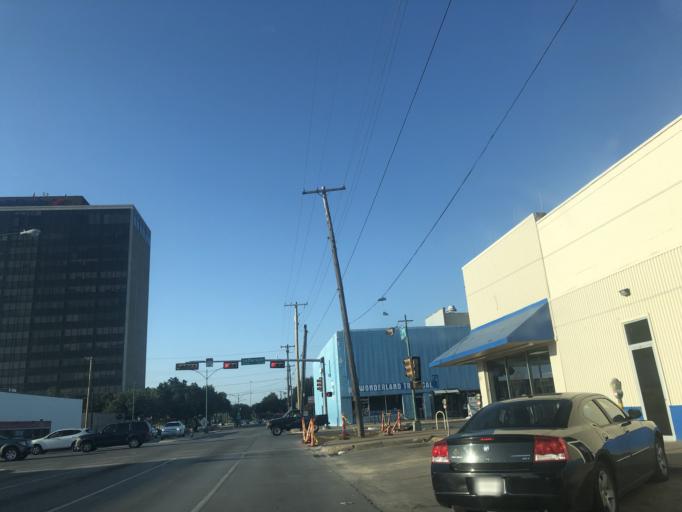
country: US
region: Texas
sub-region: Dallas County
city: Dallas
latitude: 32.7435
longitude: -96.8247
